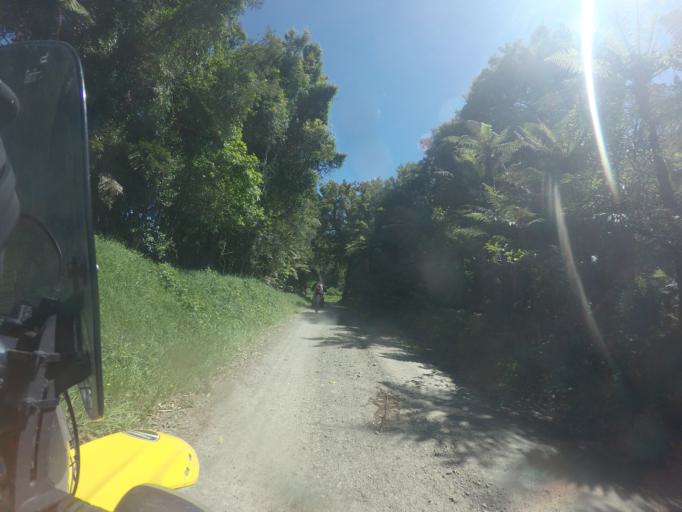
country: NZ
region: Bay of Plenty
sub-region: Opotiki District
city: Opotiki
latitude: -38.2981
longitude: 177.3351
